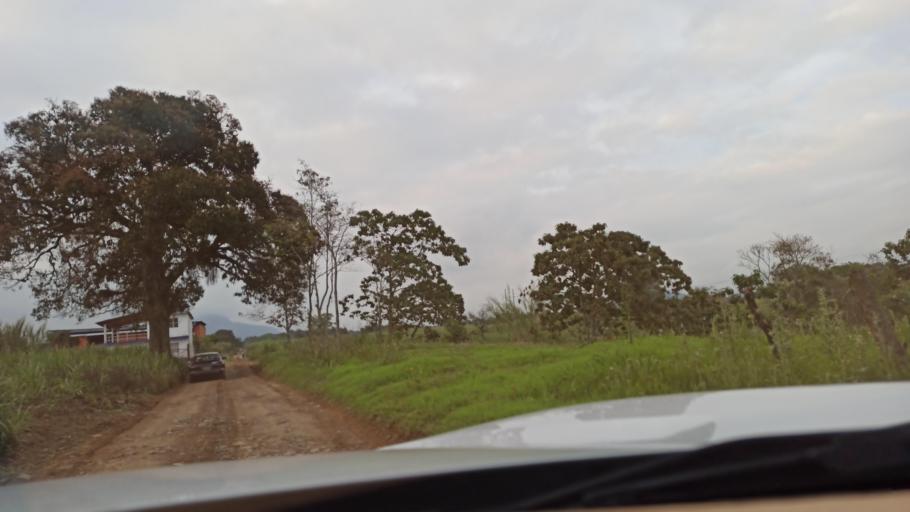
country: MX
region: Veracruz
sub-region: Fortin
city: Fraccionamiento Villas de la Llave
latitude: 18.9249
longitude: -97.0059
